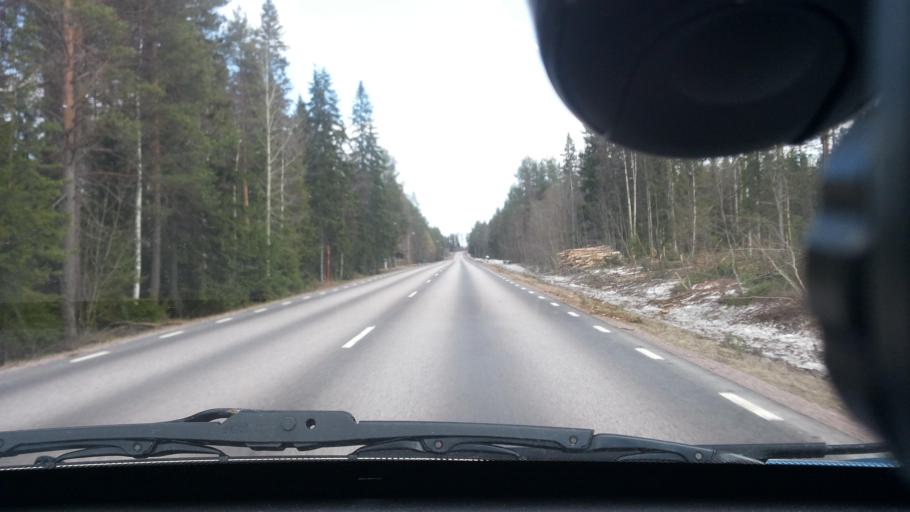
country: SE
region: Norrbotten
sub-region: Lulea Kommun
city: Gammelstad
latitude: 65.6043
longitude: 21.9711
